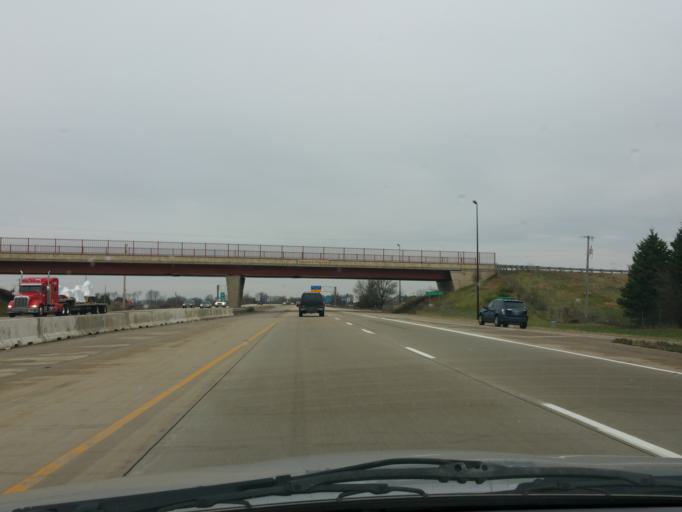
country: US
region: Wisconsin
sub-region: Rock County
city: Beloit
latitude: 42.4954
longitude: -88.9928
